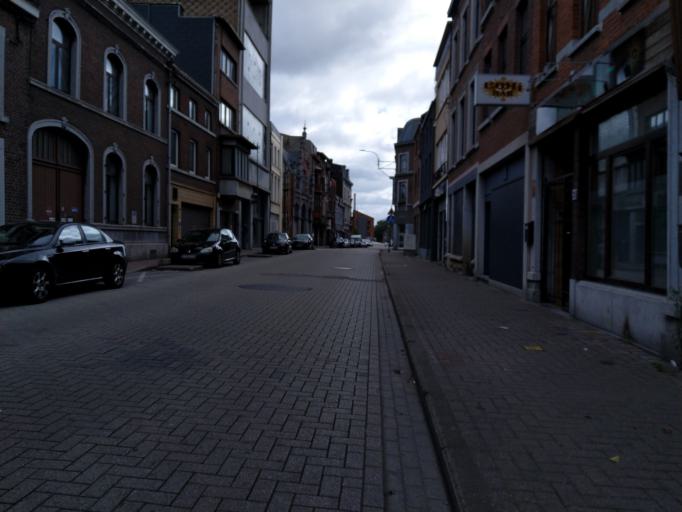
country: BE
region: Wallonia
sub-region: Province de Liege
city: Seraing
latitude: 50.6096
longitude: 5.5108
